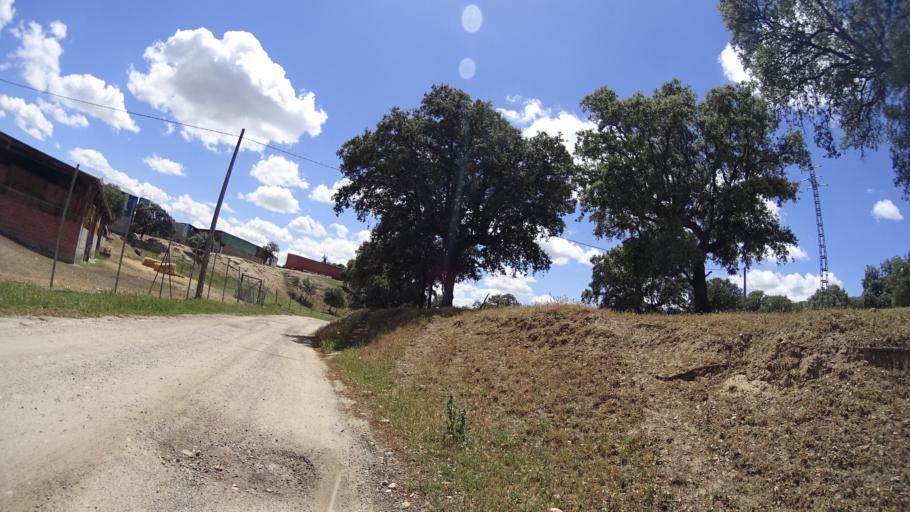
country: ES
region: Madrid
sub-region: Provincia de Madrid
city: Brunete
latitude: 40.4274
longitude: -3.9697
